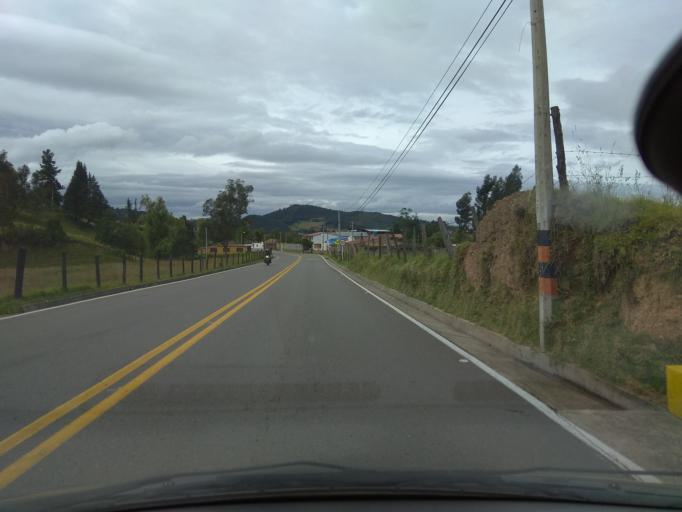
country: CO
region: Boyaca
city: Santa Rosa de Viterbo
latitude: 5.8869
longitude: -72.9793
